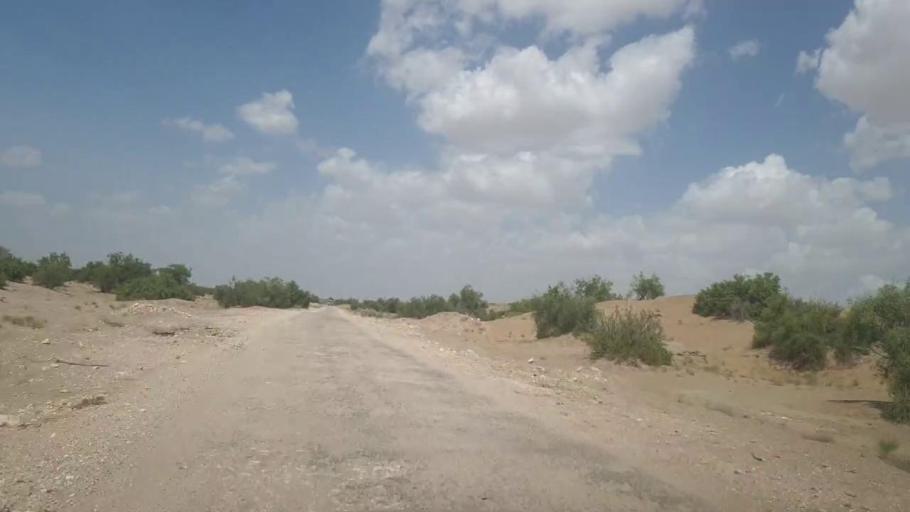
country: PK
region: Sindh
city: Kot Diji
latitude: 27.2546
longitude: 69.1657
